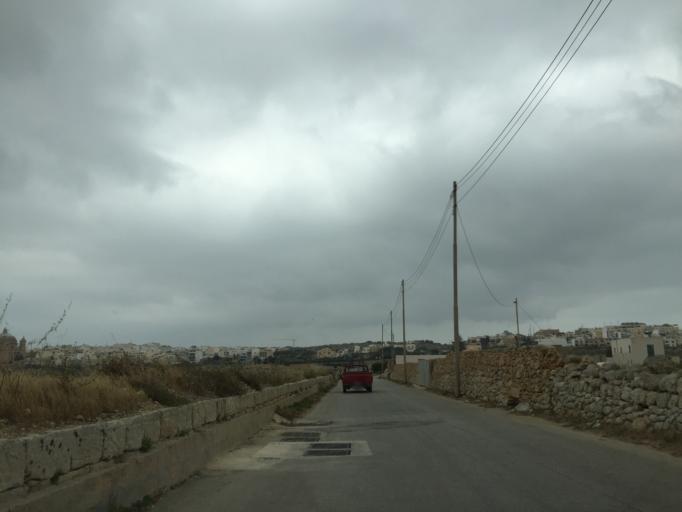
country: MT
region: L-Imgarr
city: Imgarr
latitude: 35.9134
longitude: 14.3727
